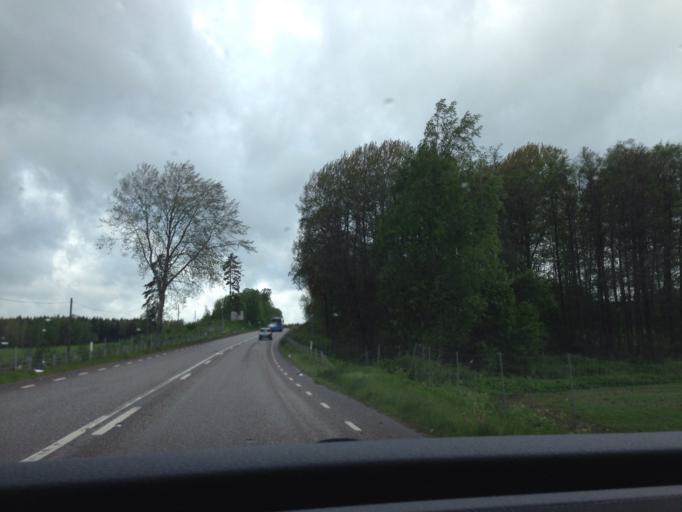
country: SE
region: Vaestra Goetaland
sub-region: Tibro Kommun
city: Tibro
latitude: 58.4173
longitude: 14.1161
